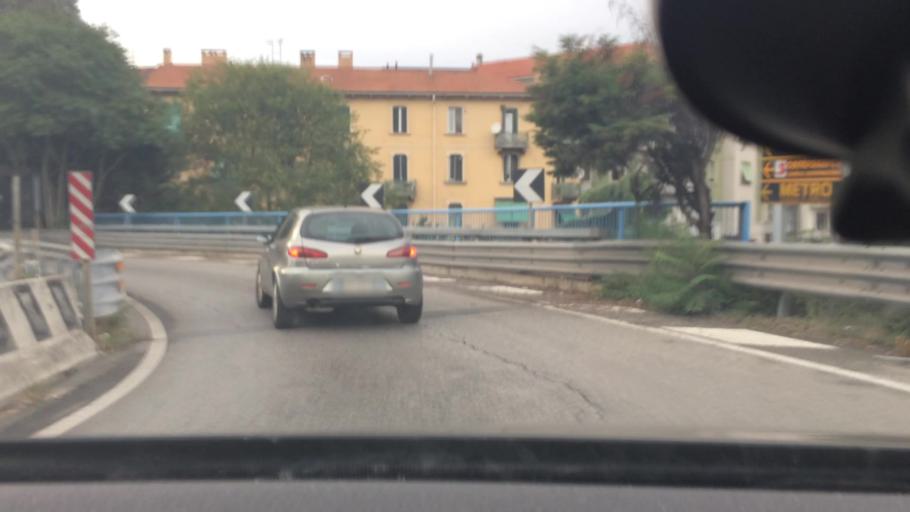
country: IT
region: Lombardy
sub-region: Citta metropolitana di Milano
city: Sesto San Giovanni
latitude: 45.5308
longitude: 9.2284
